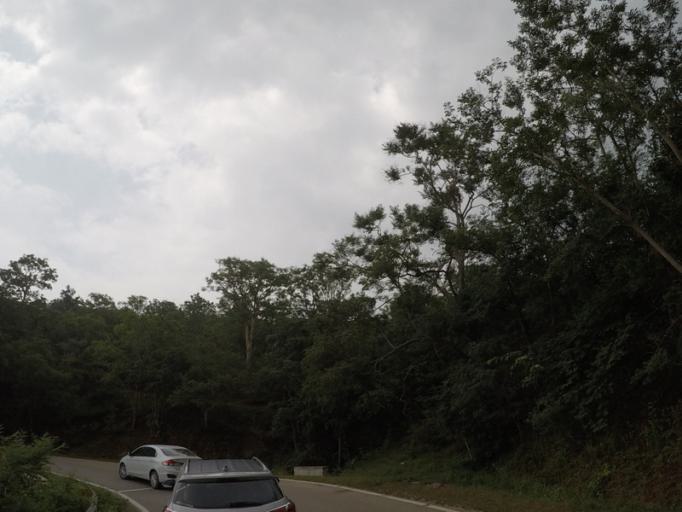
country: IN
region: Karnataka
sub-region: Chikmagalur
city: Birur
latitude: 13.5461
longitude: 75.8226
